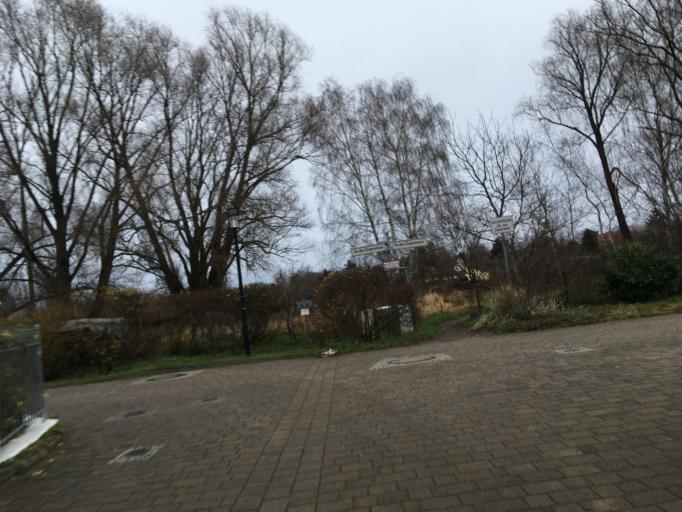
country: DE
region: Berlin
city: Wilhelmsruh
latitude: 52.5837
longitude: 13.3820
